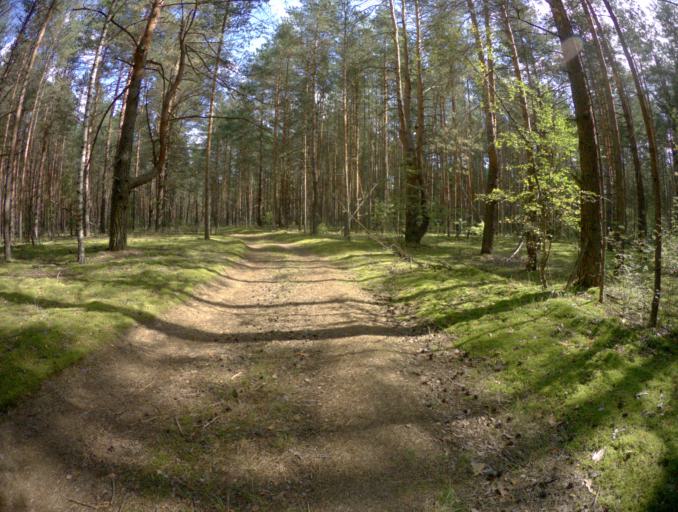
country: RU
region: Vladimir
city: Pokrov
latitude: 55.8475
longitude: 39.2573
